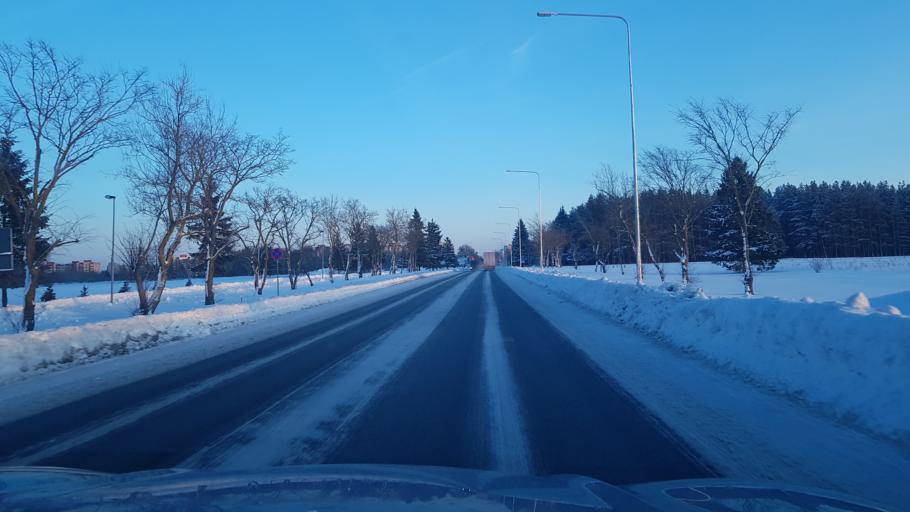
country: EE
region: Ida-Virumaa
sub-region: Narva linn
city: Narva
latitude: 59.3865
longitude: 28.1490
